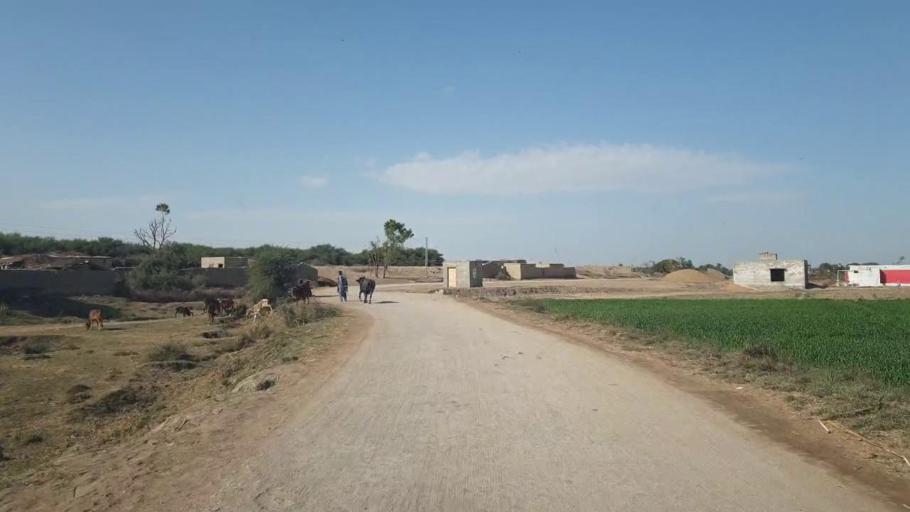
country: PK
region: Sindh
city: Hala
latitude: 25.9711
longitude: 68.3404
